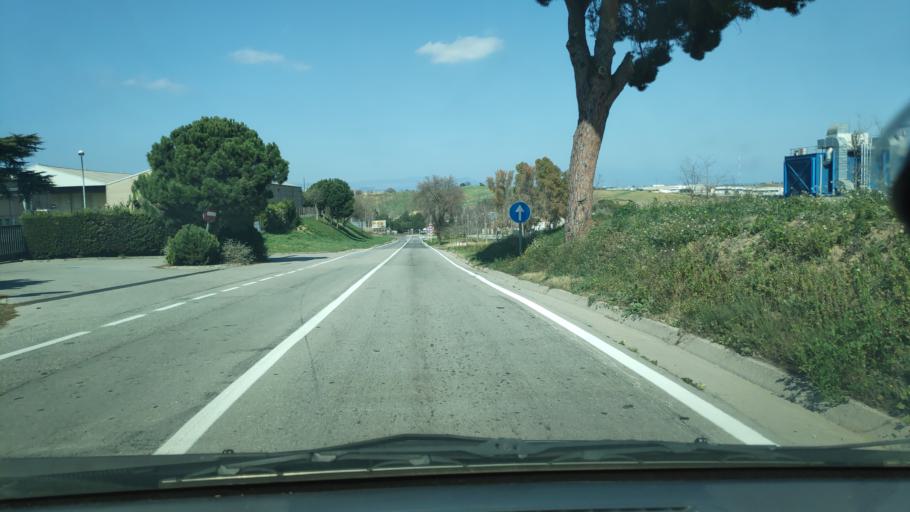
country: ES
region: Catalonia
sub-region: Provincia de Barcelona
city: Polinya
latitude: 41.5301
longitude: 2.1524
